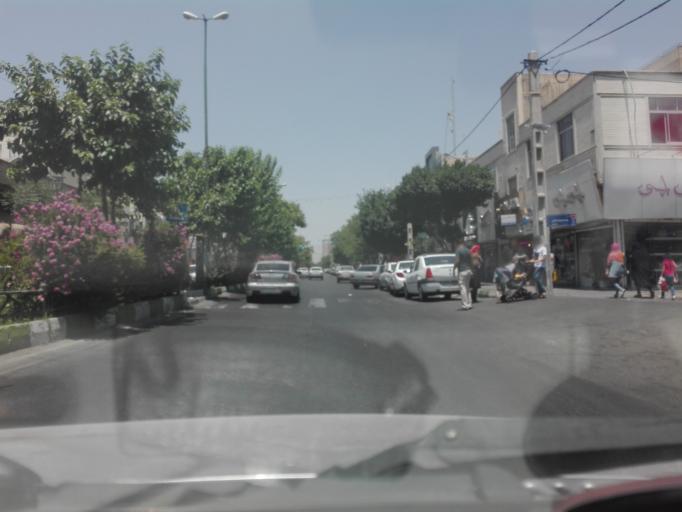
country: IR
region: Tehran
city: Shahre Jadide Andisheh
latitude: 35.7228
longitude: 50.9880
